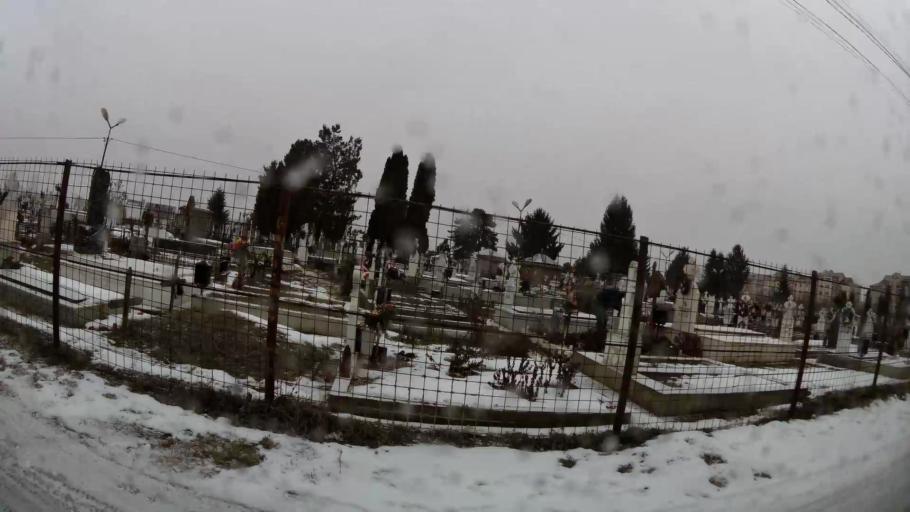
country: RO
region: Dambovita
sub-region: Municipiul Targoviste
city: Targoviste
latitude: 44.9312
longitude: 25.4376
